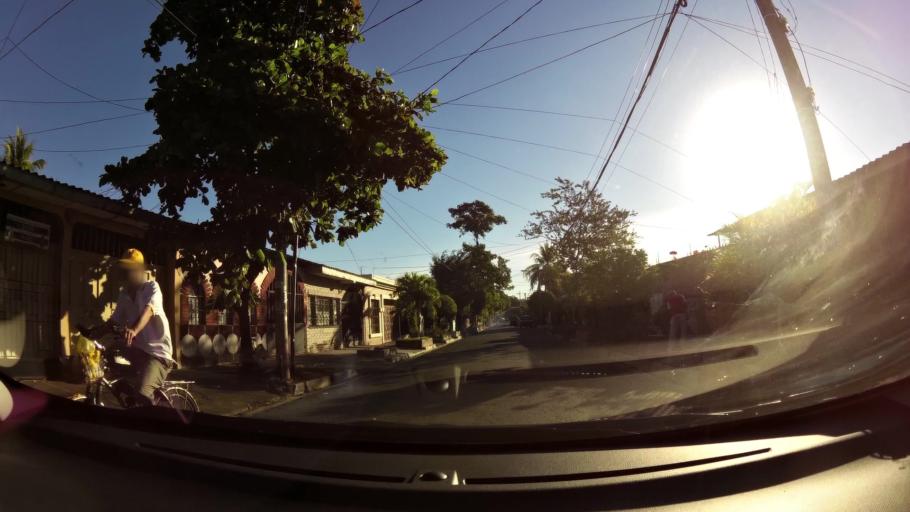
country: SV
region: San Miguel
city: San Miguel
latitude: 13.4874
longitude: -88.1707
